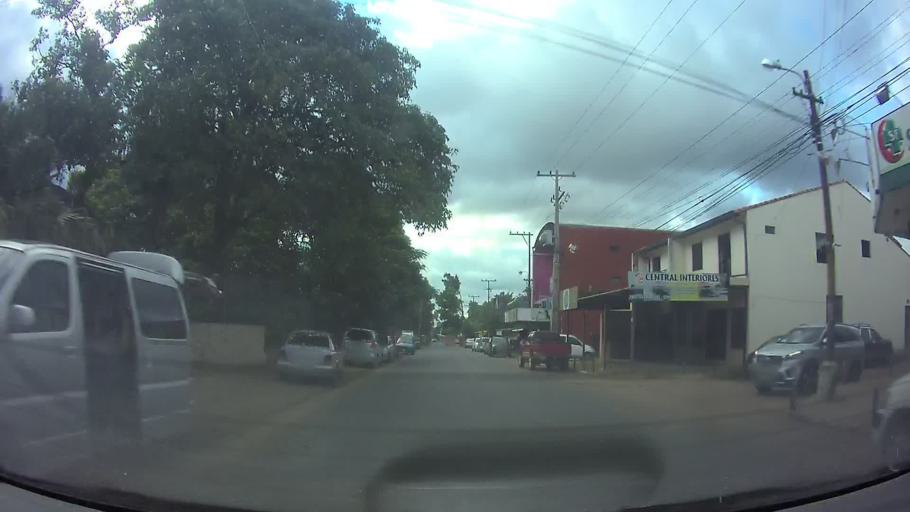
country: PY
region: Central
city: Fernando de la Mora
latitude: -25.3175
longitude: -57.5441
